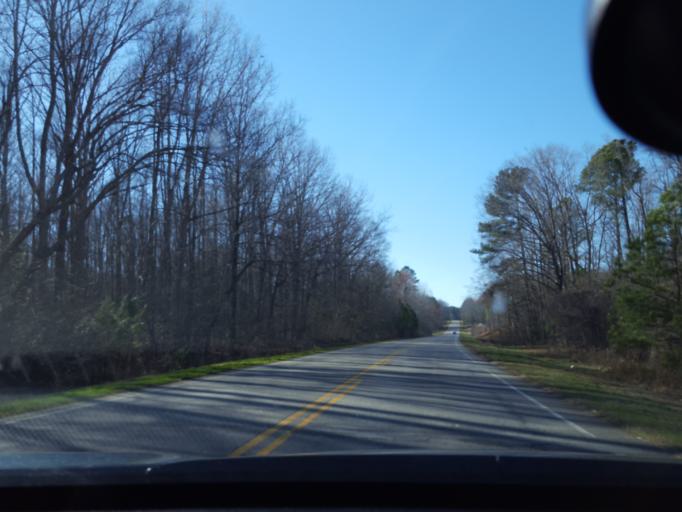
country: US
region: North Carolina
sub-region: Halifax County
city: South Rosemary
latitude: 36.4531
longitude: -77.7922
